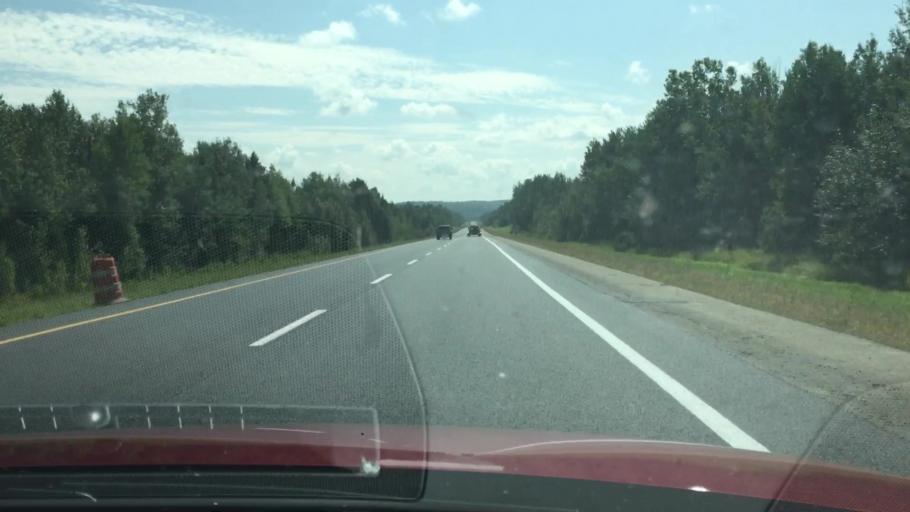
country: US
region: Maine
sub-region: Penobscot County
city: Patten
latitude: 45.8244
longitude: -68.4319
